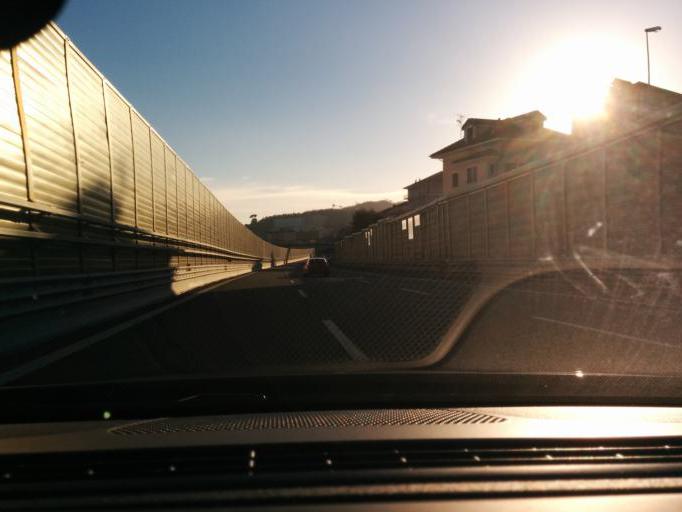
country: IT
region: Liguria
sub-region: Provincia di Genova
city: Arenzano
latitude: 44.4058
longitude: 8.6755
